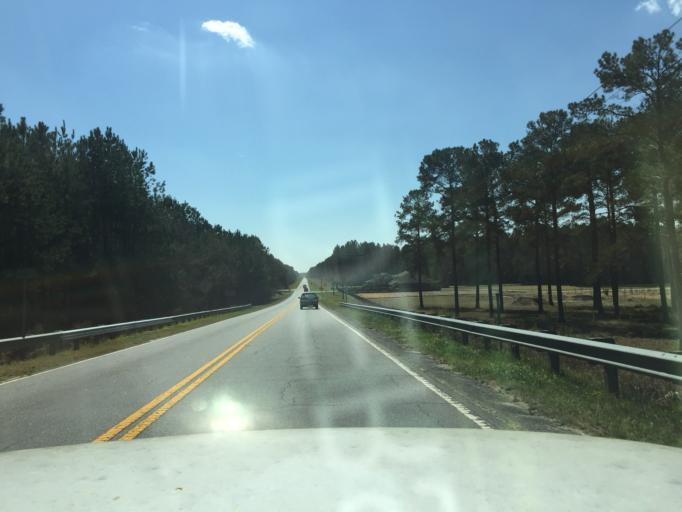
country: US
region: Georgia
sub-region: Chatham County
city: Bloomingdale
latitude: 32.0984
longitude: -81.3232
